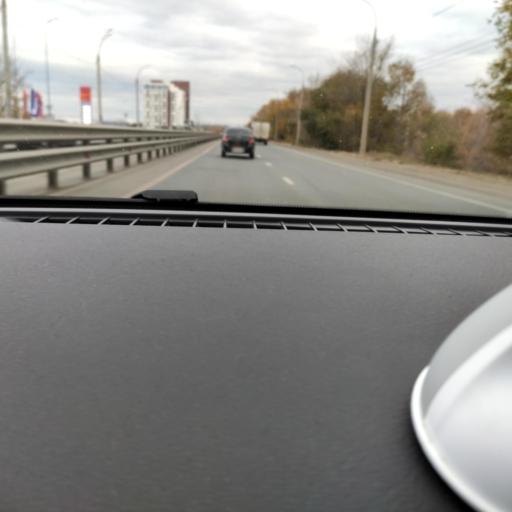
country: RU
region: Samara
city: Samara
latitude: 53.1125
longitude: 50.1656
